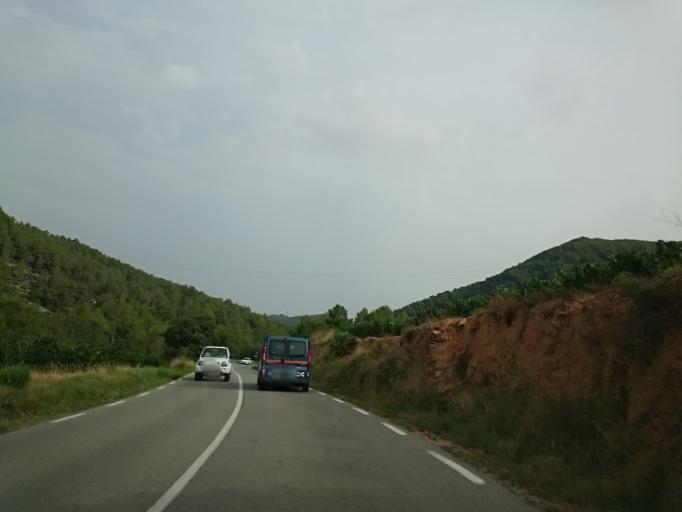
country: ES
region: Catalonia
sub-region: Provincia de Barcelona
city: Sant Pere de Ribes
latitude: 41.2783
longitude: 1.7849
